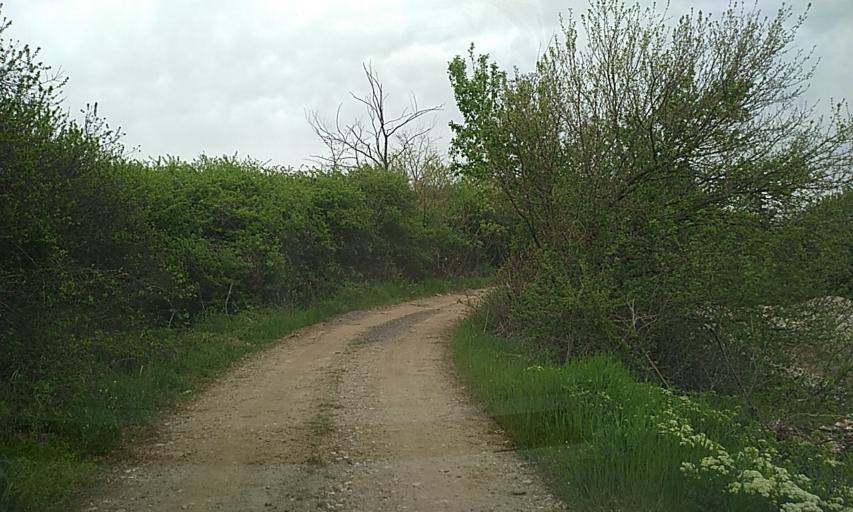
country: RS
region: Central Serbia
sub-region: Nisavski Okrug
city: Razanj
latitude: 43.5695
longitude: 21.5152
